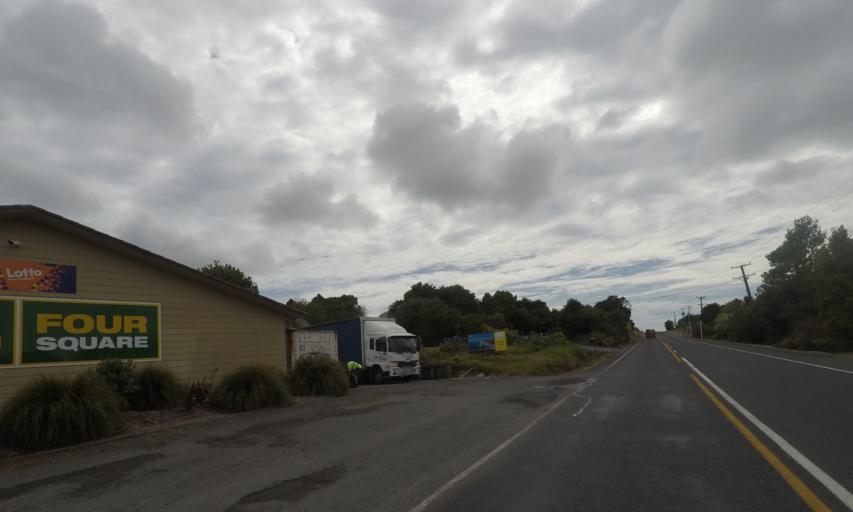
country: NZ
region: Northland
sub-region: Whangarei
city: Ruakaka
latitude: -35.7694
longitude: 174.4807
